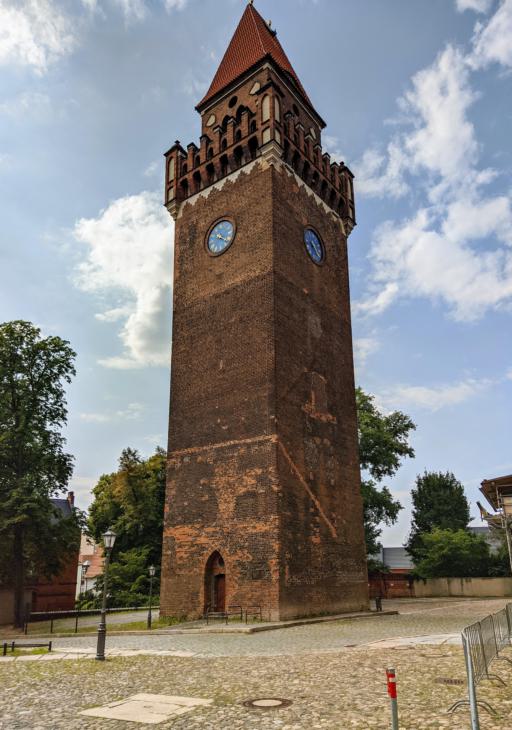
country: DE
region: Brandenburg
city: Cottbus
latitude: 51.7611
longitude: 14.3391
